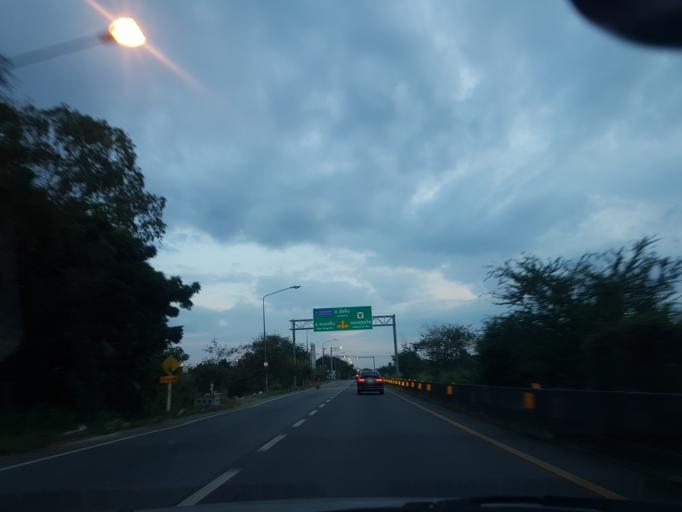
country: TH
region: Chon Buri
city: Phatthaya
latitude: 12.8910
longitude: 100.9008
